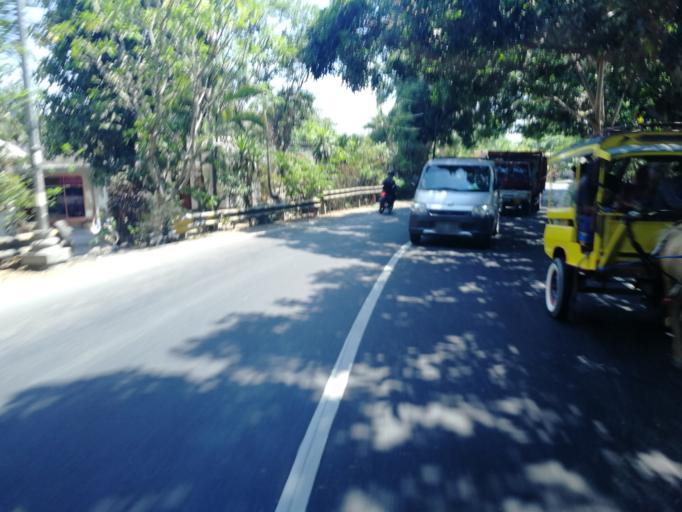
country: ID
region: West Nusa Tenggara
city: Jelateng Timur
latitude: -8.6970
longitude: 116.1058
